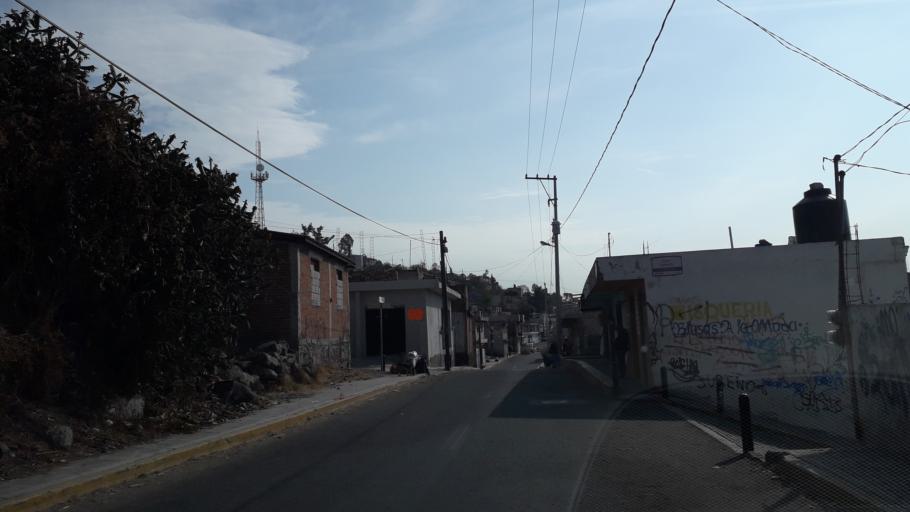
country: MX
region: Puebla
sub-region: Puebla
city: San Andres Azumiatla
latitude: 18.9036
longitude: -98.2544
